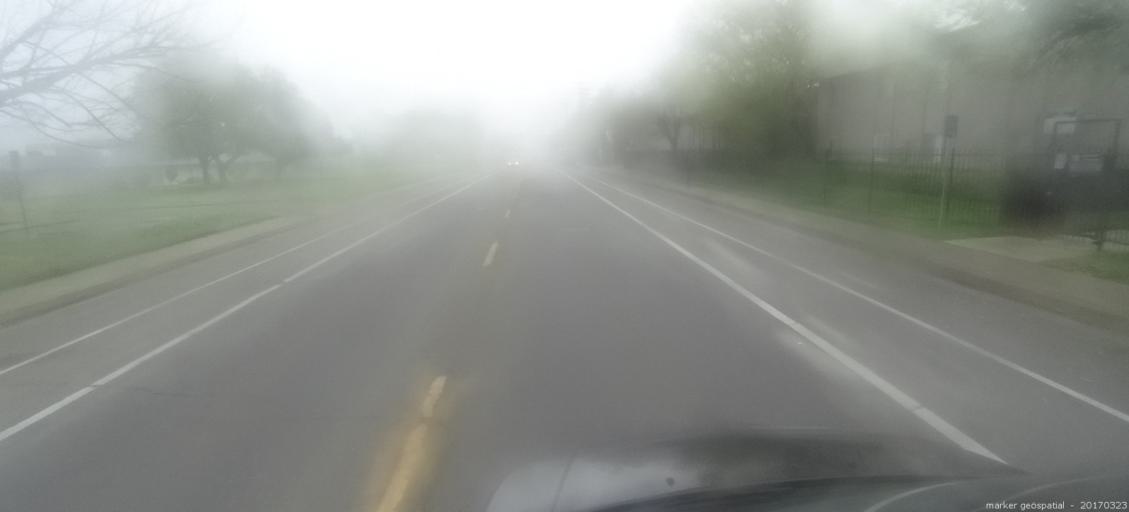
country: US
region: California
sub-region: Sacramento County
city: Florin
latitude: 38.5160
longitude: -121.4318
